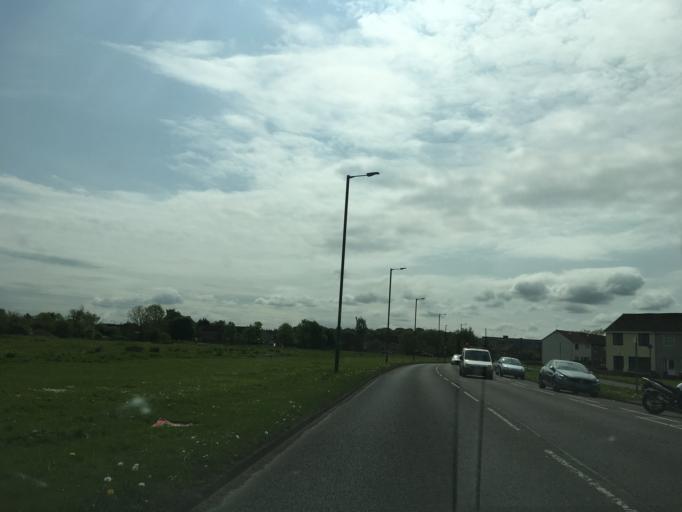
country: GB
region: Scotland
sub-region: Stirling
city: Stirling
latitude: 56.1065
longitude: -3.9253
